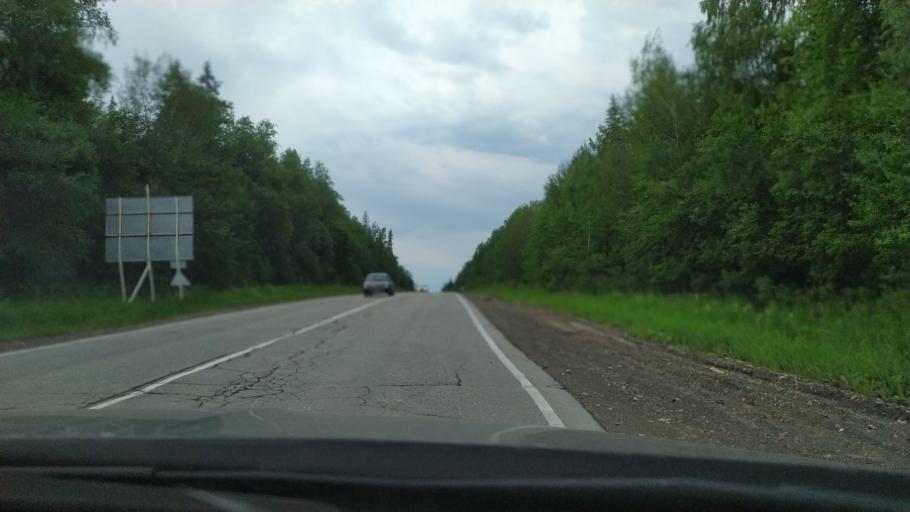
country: RU
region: Perm
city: Gremyachinsk
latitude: 58.4302
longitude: 57.8842
